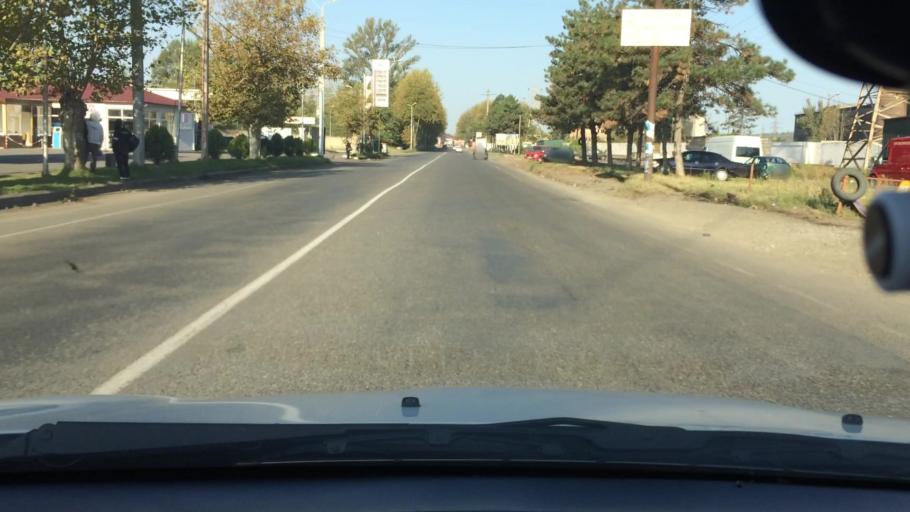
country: GE
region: Imereti
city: Zestap'oni
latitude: 42.1174
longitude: 43.0191
